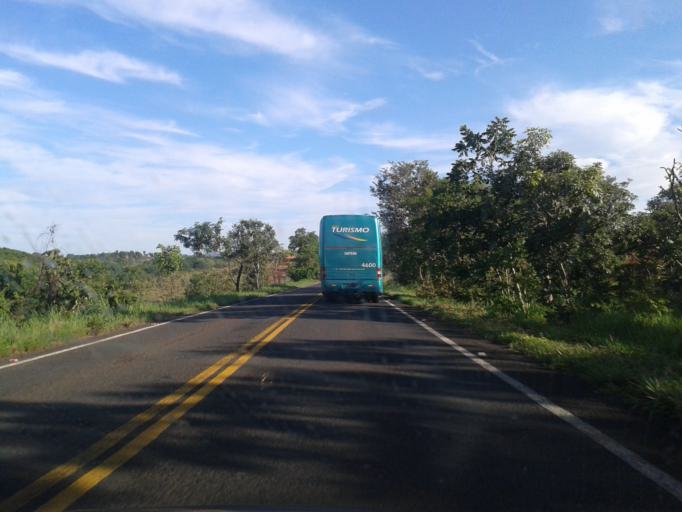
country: BR
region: Minas Gerais
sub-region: Tupaciguara
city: Tupaciguara
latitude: -18.2960
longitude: -48.5632
